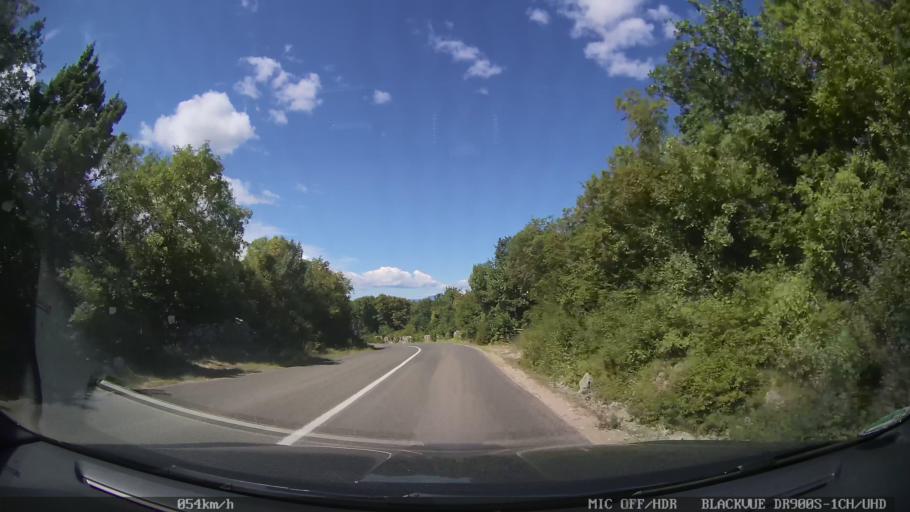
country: HR
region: Primorsko-Goranska
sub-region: Grad Krk
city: Krk
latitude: 45.0495
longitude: 14.5077
